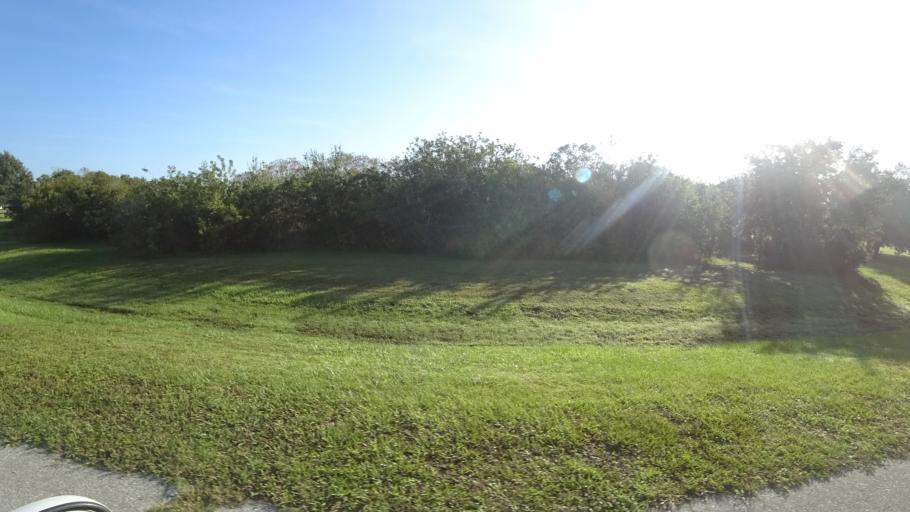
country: US
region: Florida
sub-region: Hillsborough County
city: Sun City Center
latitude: 27.5536
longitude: -82.3538
